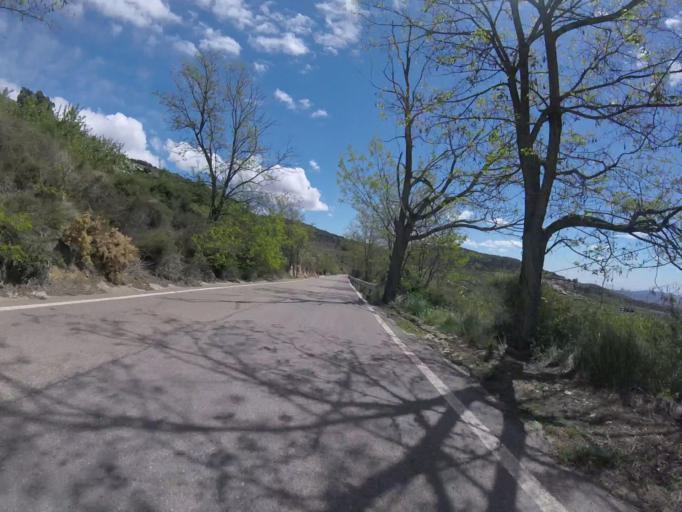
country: ES
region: Valencia
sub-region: Provincia de Castello
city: Sierra-Engarceran
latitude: 40.2756
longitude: -0.0295
